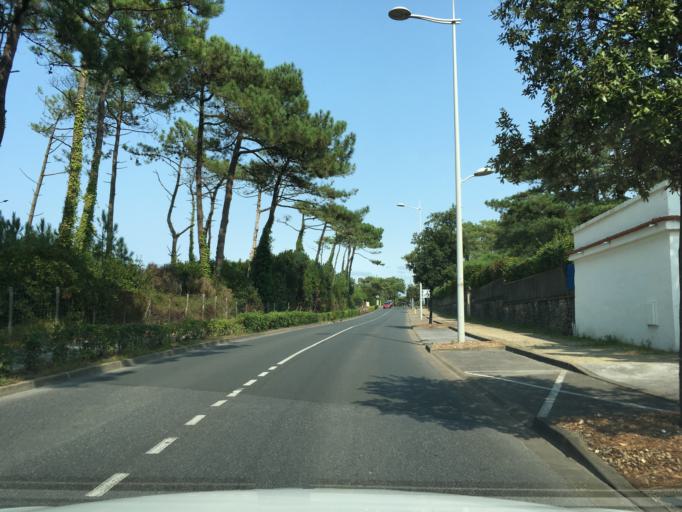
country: FR
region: Aquitaine
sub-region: Departement des Pyrenees-Atlantiques
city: Biarritz
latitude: 43.5078
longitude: -1.5328
